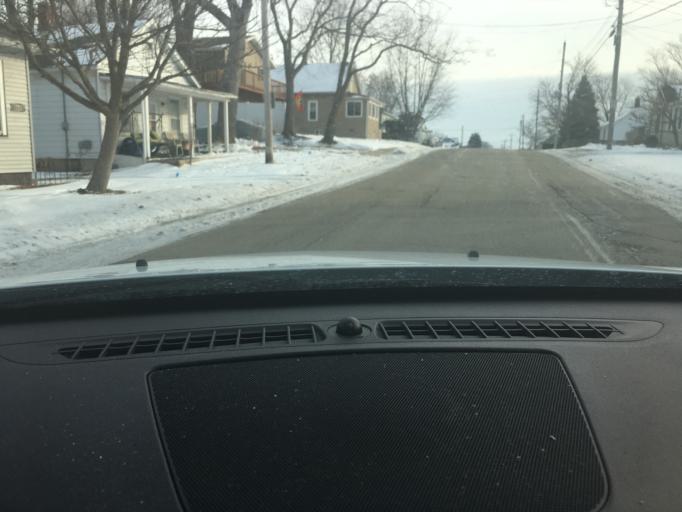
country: US
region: Illinois
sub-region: LaSalle County
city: Peru
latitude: 41.3306
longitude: -89.1154
